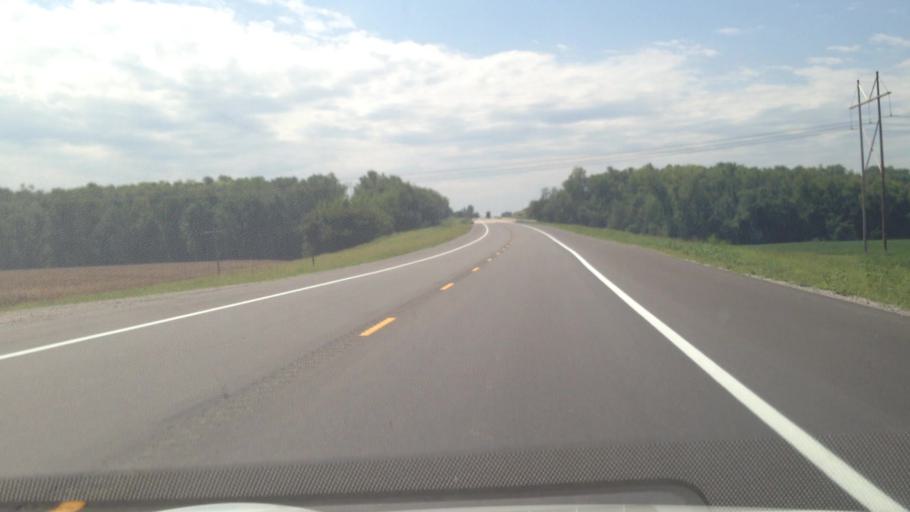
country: US
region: Kansas
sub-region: Anderson County
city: Garnett
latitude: 38.3372
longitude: -95.2489
